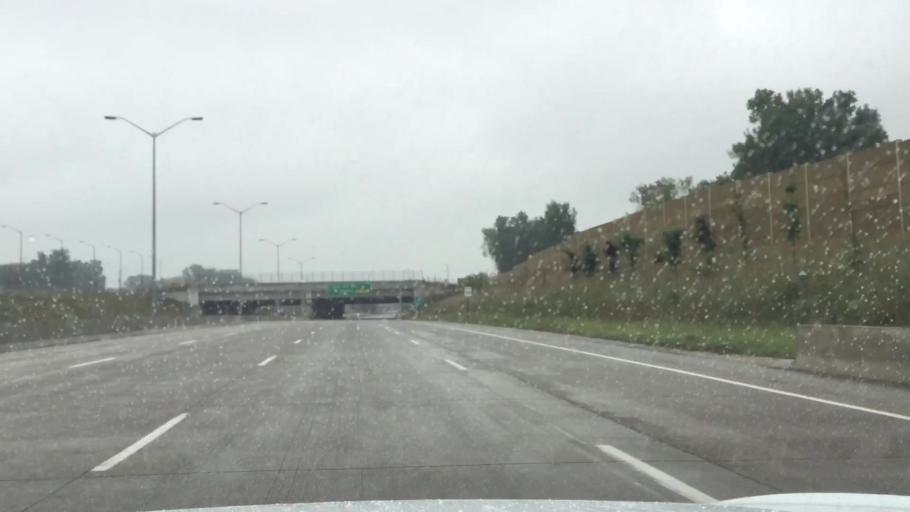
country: CA
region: Ontario
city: Windsor
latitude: 42.2598
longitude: -83.0411
